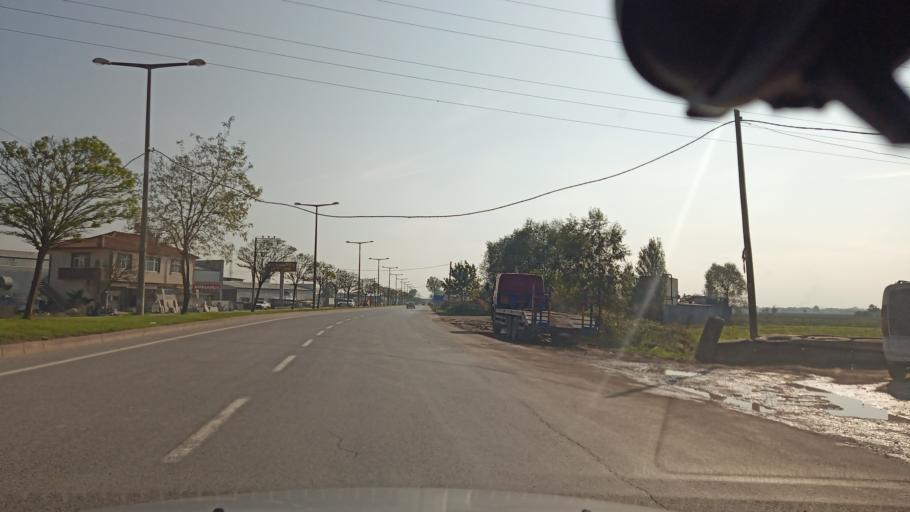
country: TR
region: Sakarya
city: Adapazari
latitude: 40.8210
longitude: 30.3971
